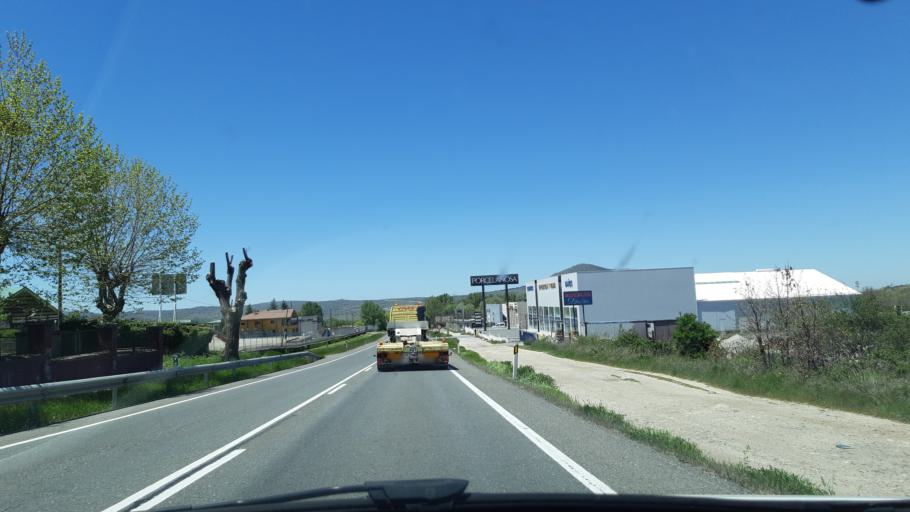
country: ES
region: Castille and Leon
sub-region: Provincia de Avila
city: Peguerinos
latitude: 40.7178
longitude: -4.2078
